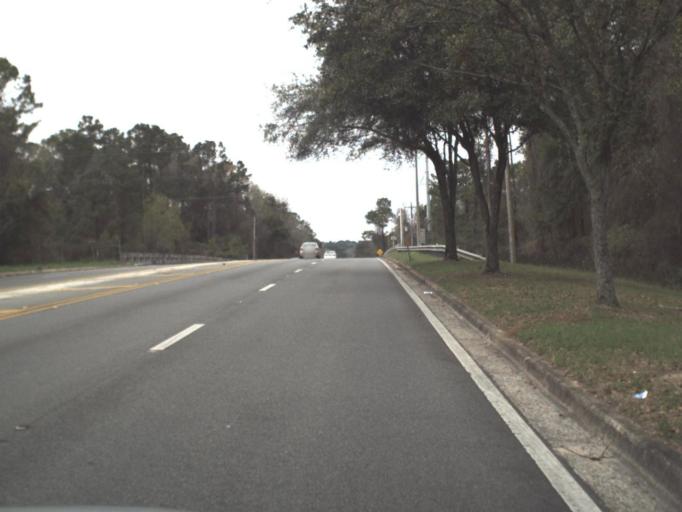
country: US
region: Florida
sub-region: Leon County
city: Tallahassee
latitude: 30.4921
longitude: -84.2772
